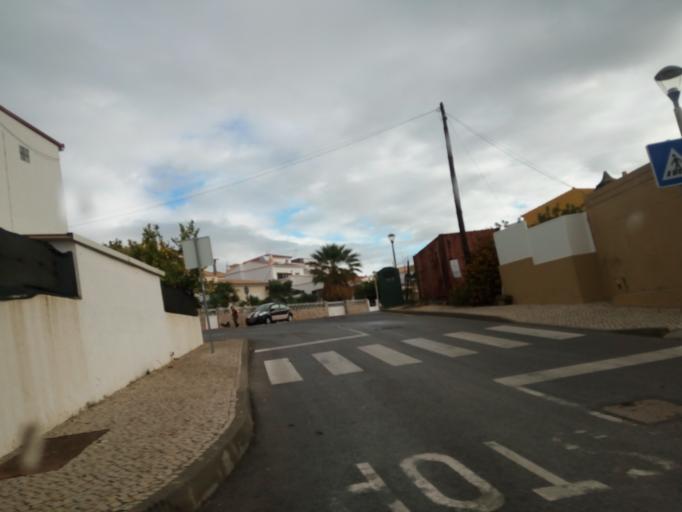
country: PT
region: Faro
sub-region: Loule
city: Loule
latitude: 37.1207
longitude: -8.0130
